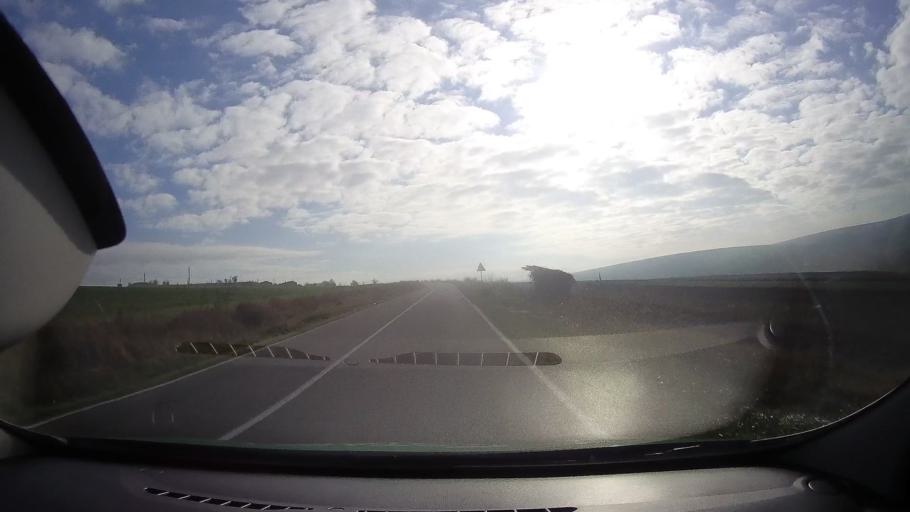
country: RO
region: Tulcea
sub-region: Comuna Bestepe
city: Bestepe
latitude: 45.0833
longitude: 29.0227
